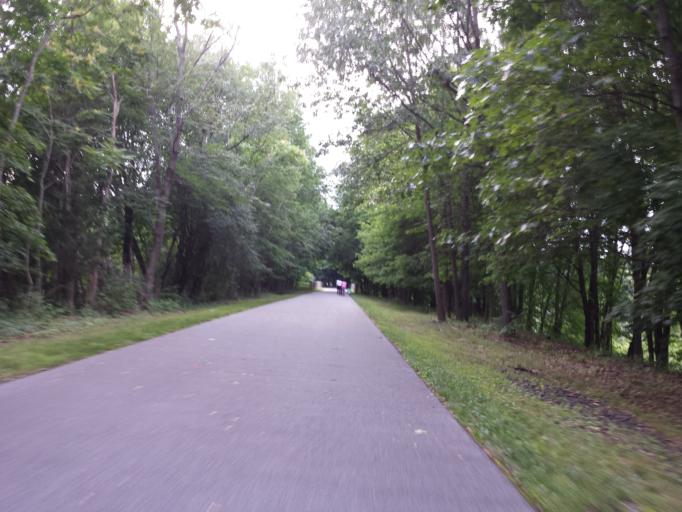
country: US
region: New York
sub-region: Dutchess County
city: Arlington
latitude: 41.7157
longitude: -73.8996
